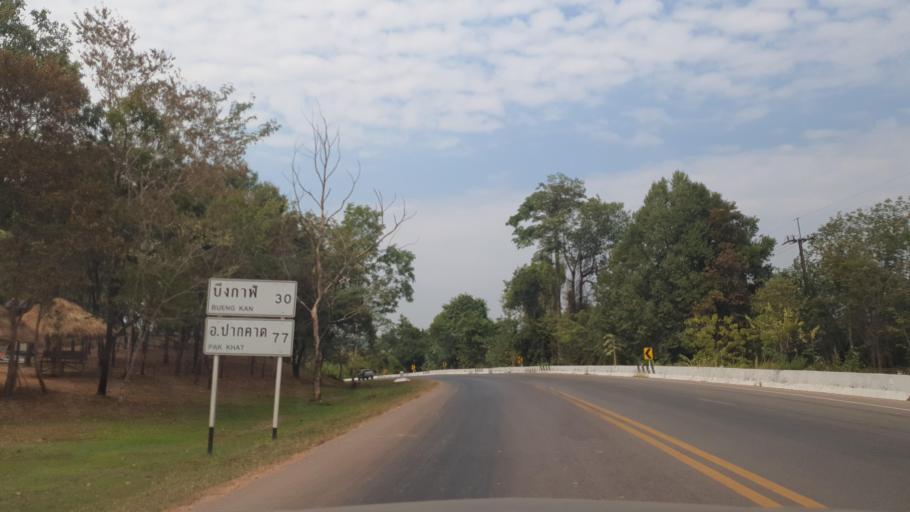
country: TH
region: Changwat Bueng Kan
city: Bung Khla
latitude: 18.2902
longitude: 103.8908
